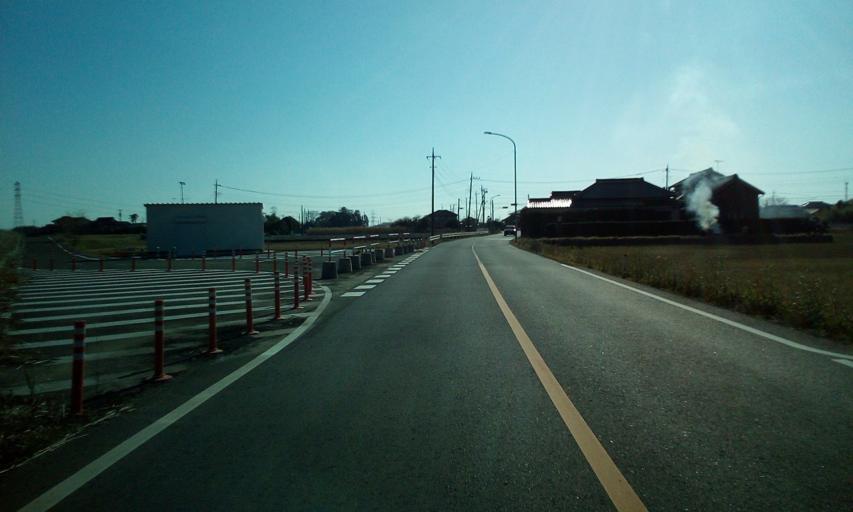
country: JP
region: Ibaraki
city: Sakai
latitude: 36.0700
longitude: 139.7800
